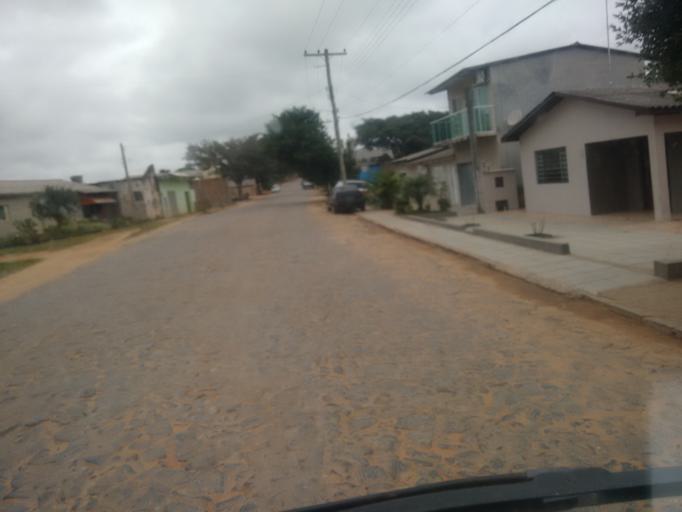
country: BR
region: Rio Grande do Sul
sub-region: Camaqua
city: Camaqua
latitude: -30.7917
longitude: -51.8314
